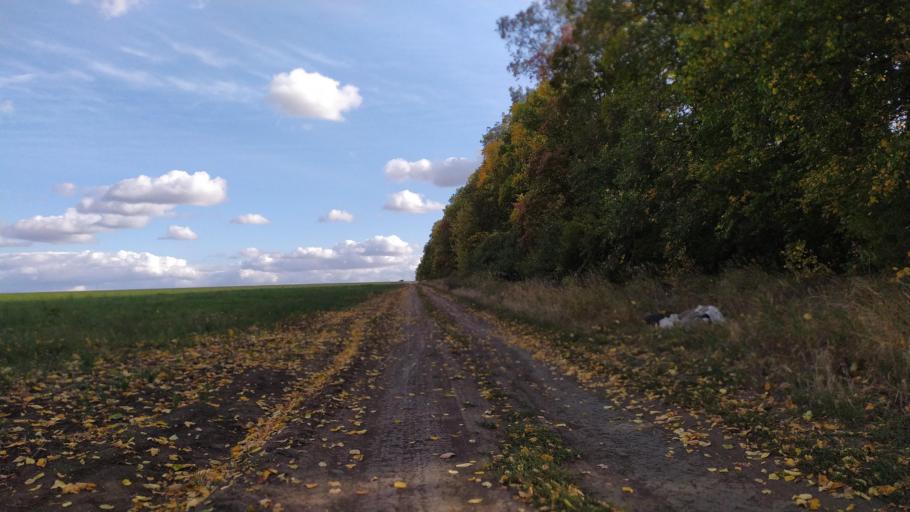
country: RU
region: Kursk
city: Kursk
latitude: 51.6201
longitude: 36.1625
